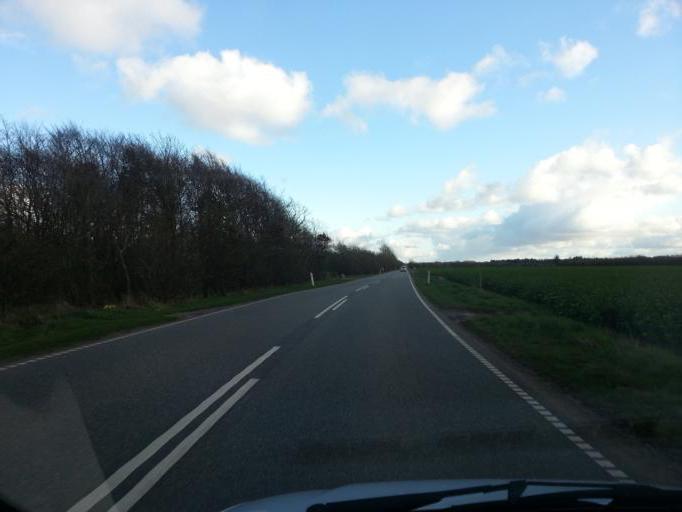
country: DK
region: Central Jutland
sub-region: Ringkobing-Skjern Kommune
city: Tarm
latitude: 55.8838
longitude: 8.5257
